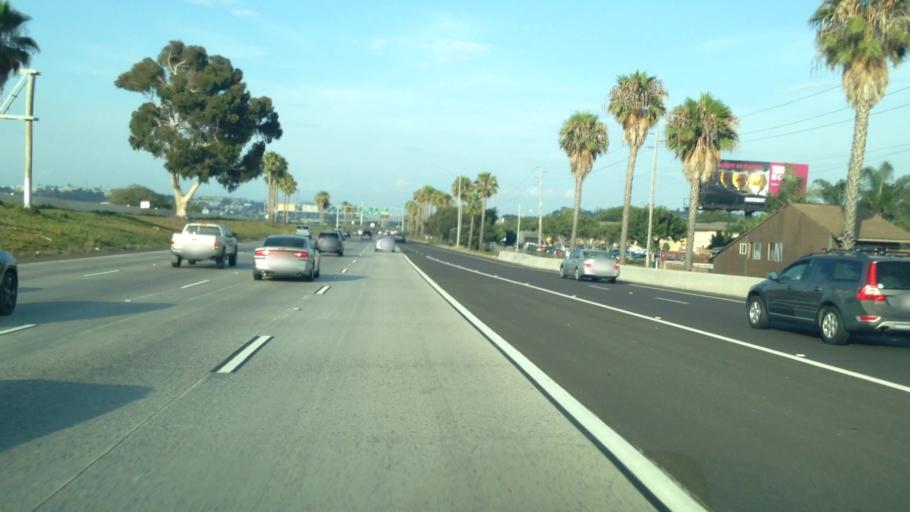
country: US
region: California
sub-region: San Diego County
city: San Diego
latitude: 32.7571
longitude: -117.2195
